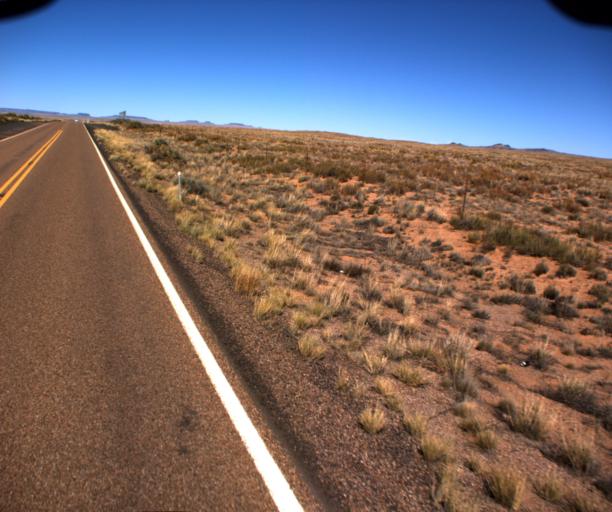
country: US
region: Arizona
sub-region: Navajo County
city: Holbrook
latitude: 35.0050
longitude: -110.0896
